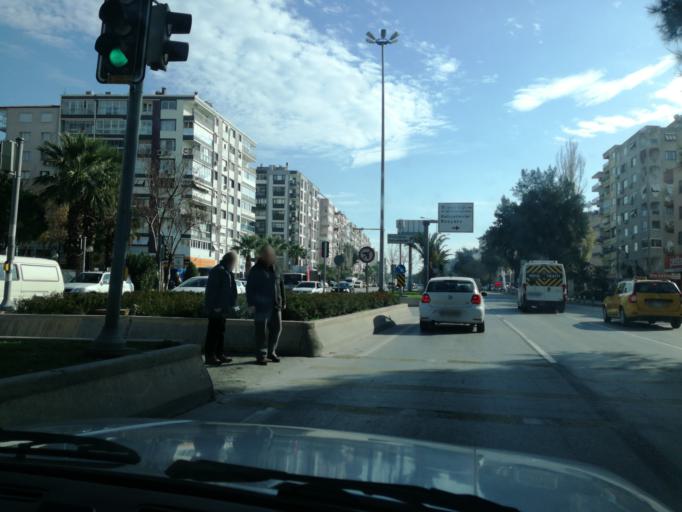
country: TR
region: Izmir
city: Izmir
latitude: 38.4031
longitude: 27.1237
